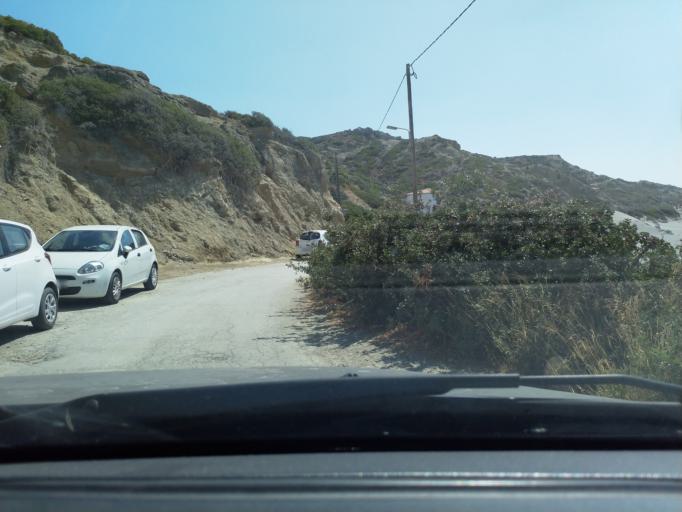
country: GR
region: Crete
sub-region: Nomos Rethymnis
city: Agia Foteini
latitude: 35.1384
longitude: 24.5291
